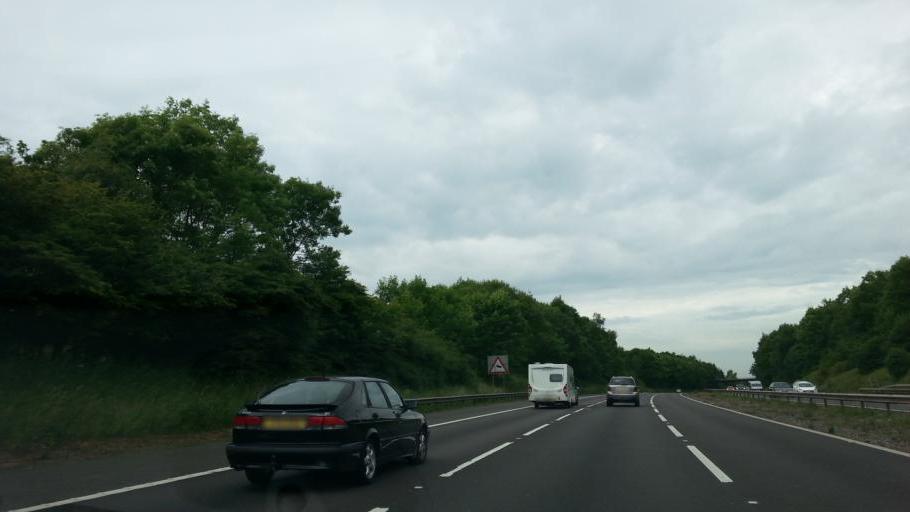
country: GB
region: England
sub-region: Worcestershire
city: Barnt Green
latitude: 52.3531
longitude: -2.0067
